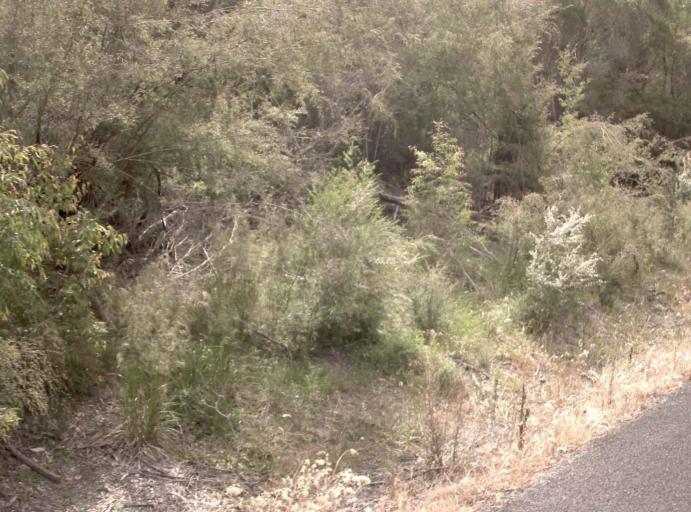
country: AU
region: New South Wales
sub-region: Bega Valley
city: Eden
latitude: -37.4677
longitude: 149.5881
